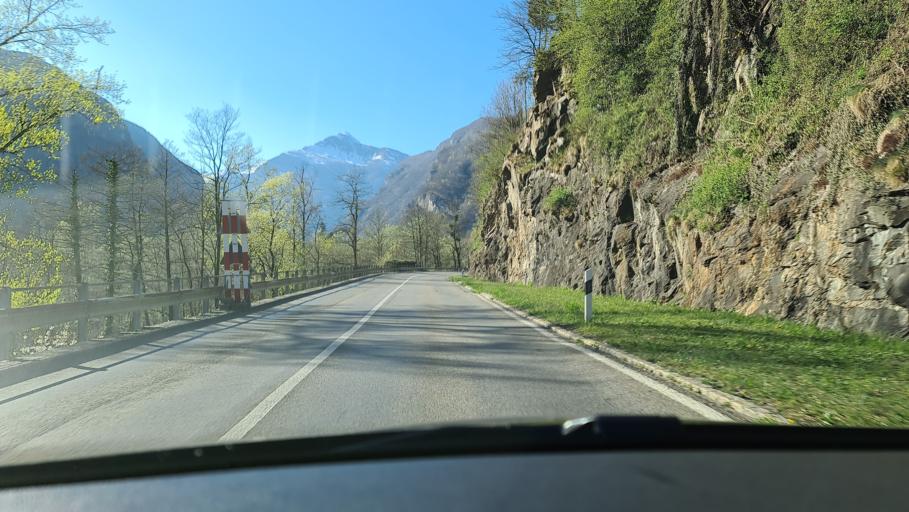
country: CH
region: Ticino
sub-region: Vallemaggia District
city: Cevio
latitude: 46.2797
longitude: 8.6728
